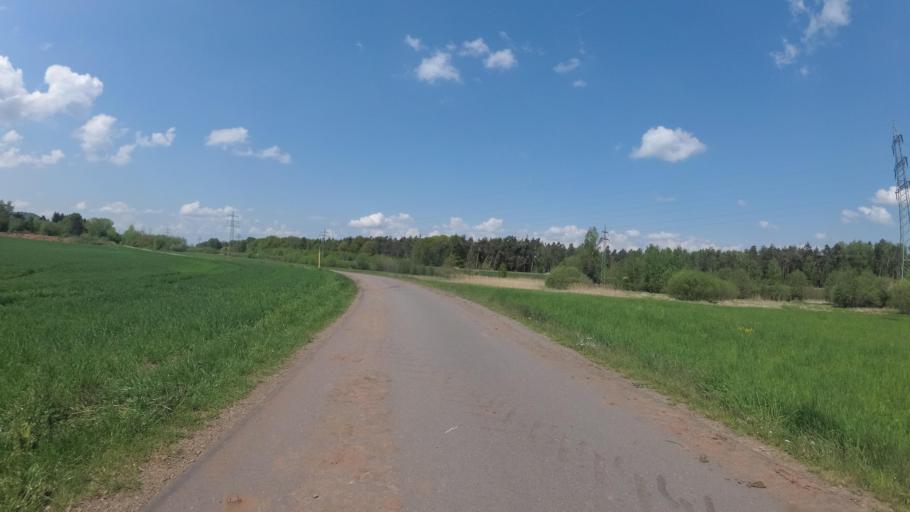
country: DE
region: Rheinland-Pfalz
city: Kindsbach
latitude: 49.4200
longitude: 7.6010
